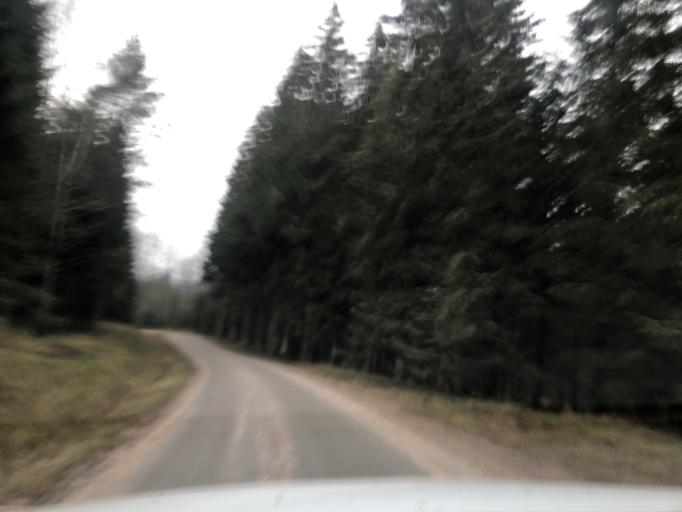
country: SE
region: Vaestra Goetaland
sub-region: Ulricehamns Kommun
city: Ulricehamn
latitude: 57.8707
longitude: 13.5584
